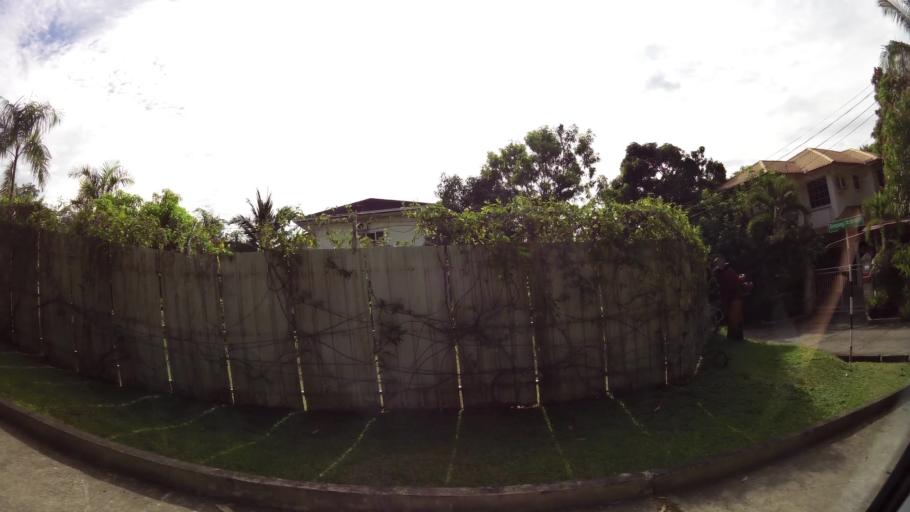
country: BN
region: Brunei and Muara
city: Bandar Seri Begawan
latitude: 4.9019
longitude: 114.8842
